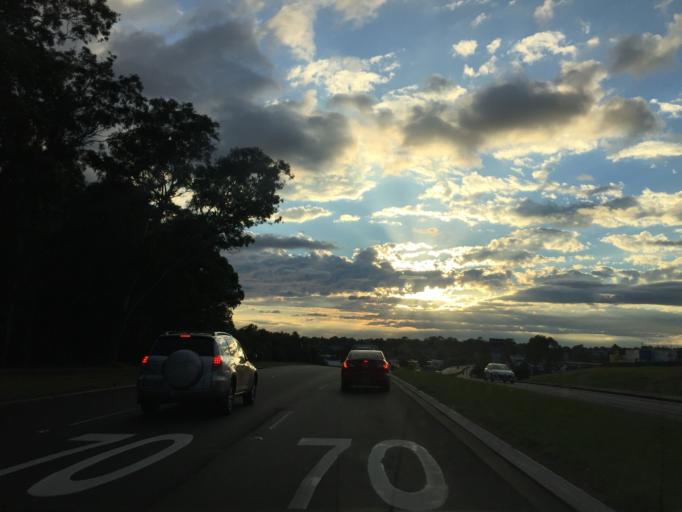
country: AU
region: New South Wales
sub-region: Shellharbour
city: Barrack Heights
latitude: -34.5650
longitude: 150.8278
